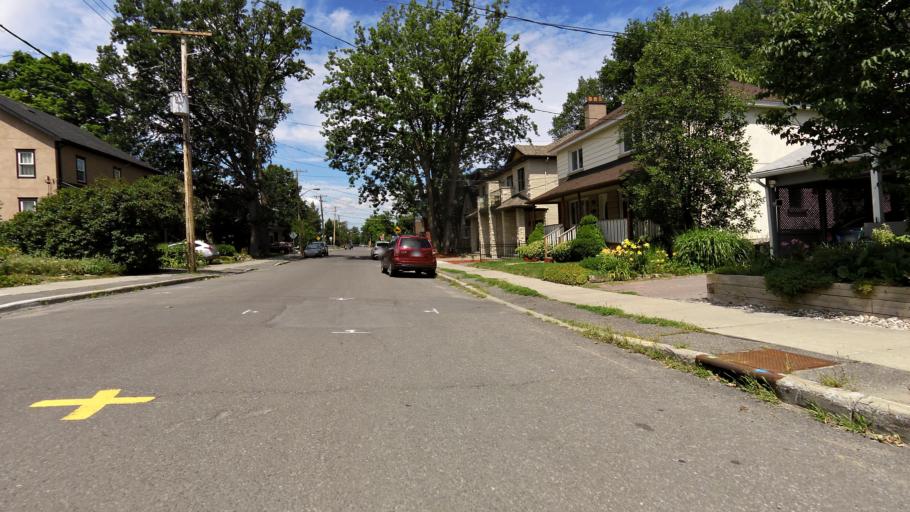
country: CA
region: Ontario
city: Ottawa
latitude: 45.4031
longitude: -75.7439
